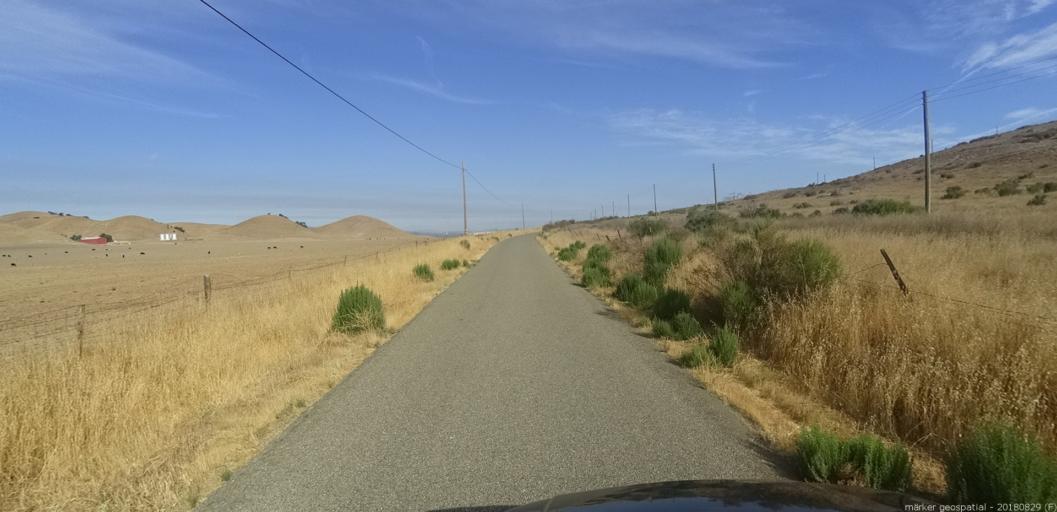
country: US
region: California
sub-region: Monterey County
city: King City
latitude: 36.0407
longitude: -120.9723
